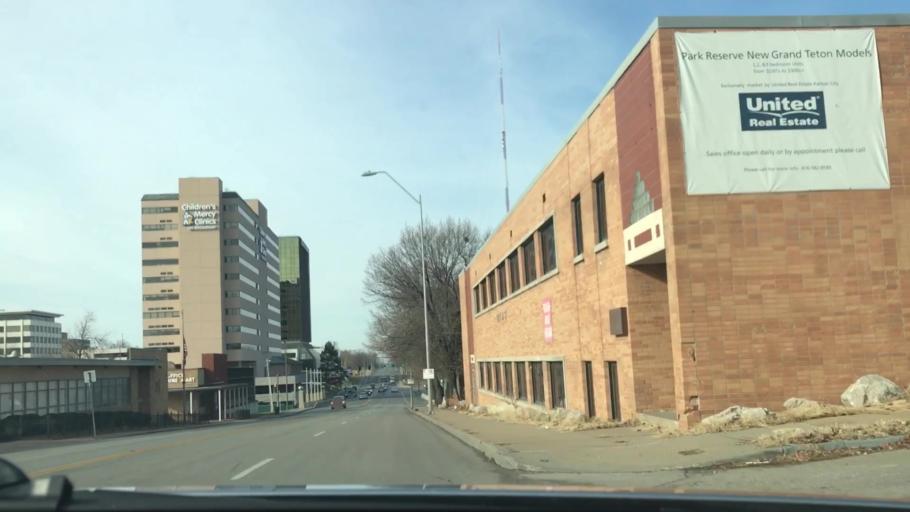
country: US
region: Missouri
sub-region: Jackson County
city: Kansas City
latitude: 39.0711
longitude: -94.5866
